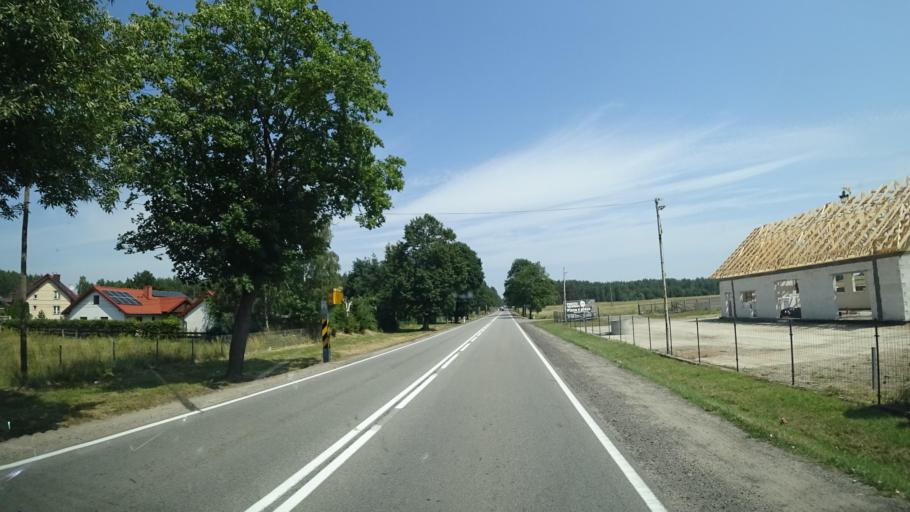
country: PL
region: Pomeranian Voivodeship
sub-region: Powiat koscierski
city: Koscierzyna
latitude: 54.1657
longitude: 18.0431
